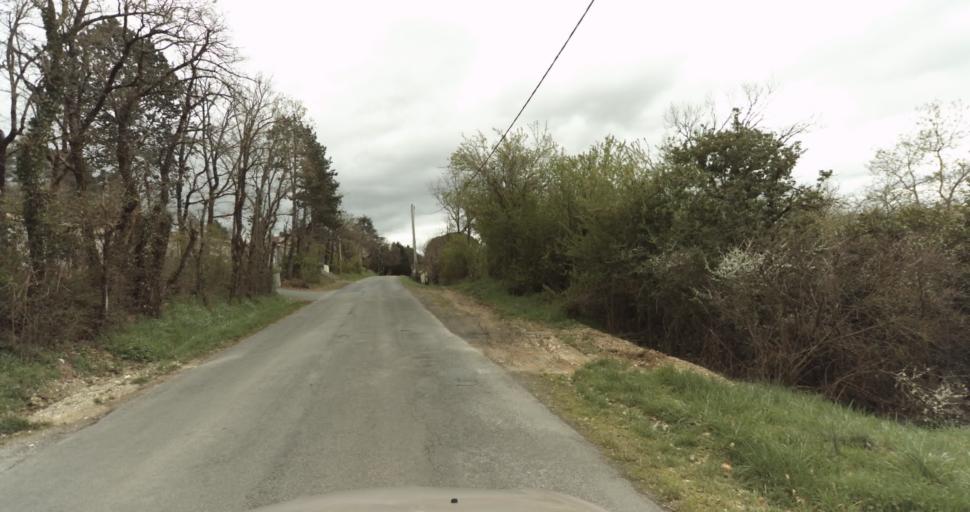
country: FR
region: Midi-Pyrenees
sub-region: Departement du Tarn
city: Puygouzon
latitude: 43.9029
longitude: 2.1724
